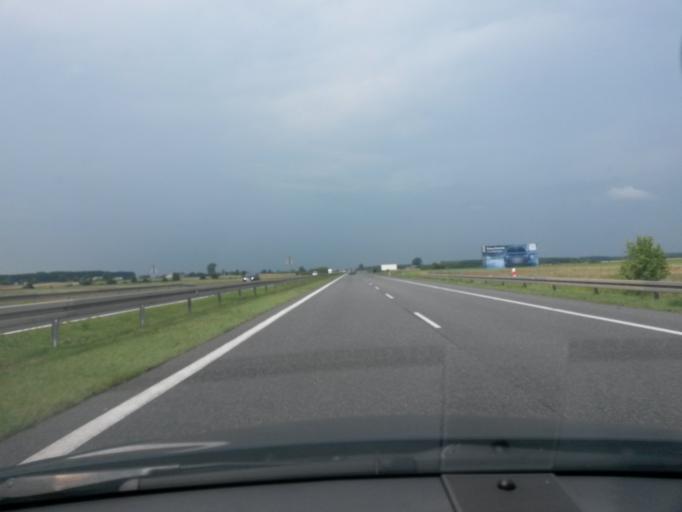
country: PL
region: Lodz Voivodeship
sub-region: Powiat piotrkowski
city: Wola Krzysztoporska
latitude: 51.3657
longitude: 19.6142
